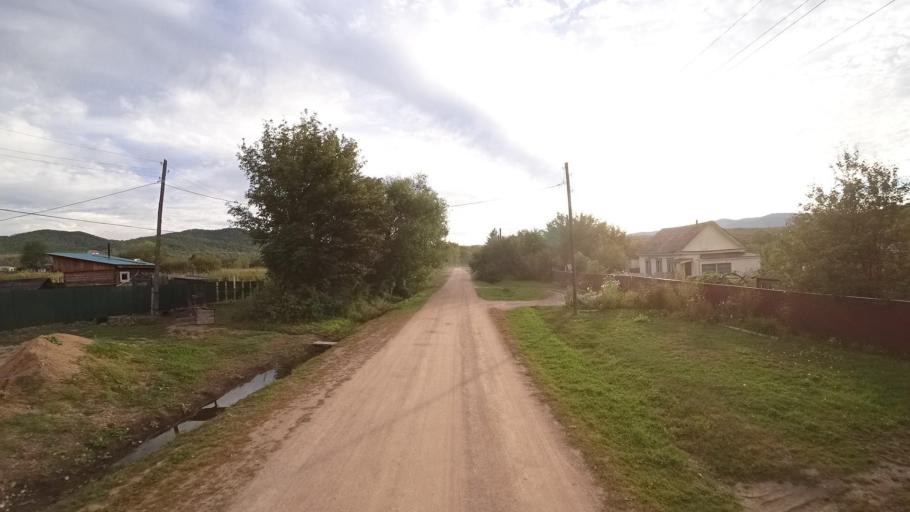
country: RU
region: Primorskiy
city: Yakovlevka
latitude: 44.4185
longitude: 133.4499
